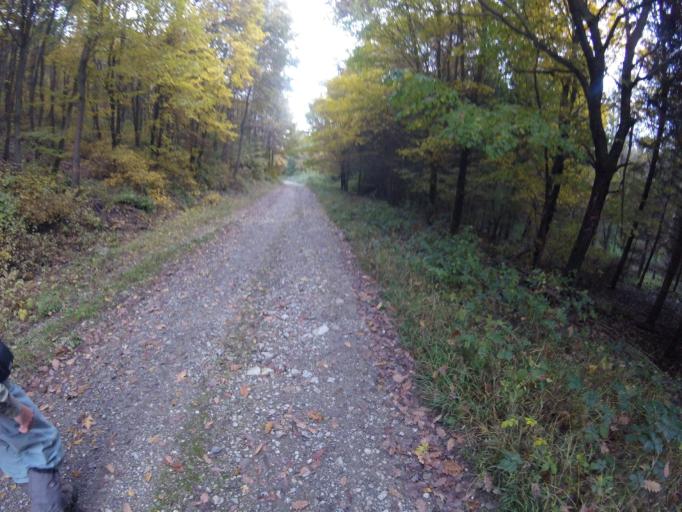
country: HU
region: Borsod-Abauj-Zemplen
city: Putnok
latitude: 48.2425
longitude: 20.4296
